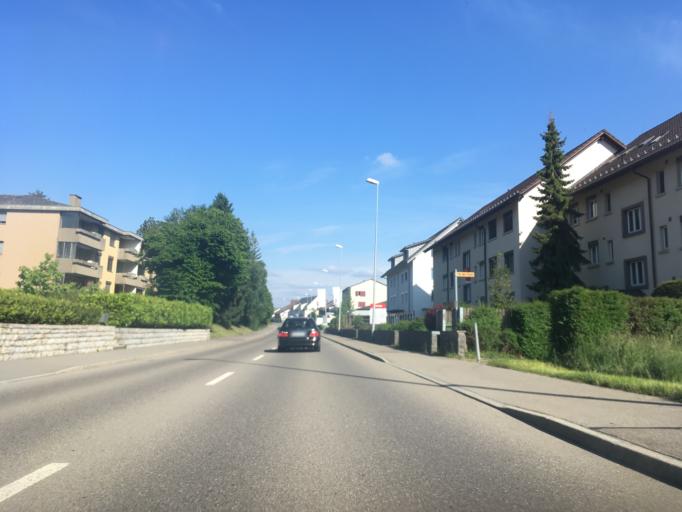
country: CH
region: Zurich
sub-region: Bezirk Dielsdorf
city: Otelfingen
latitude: 47.5001
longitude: 8.4086
